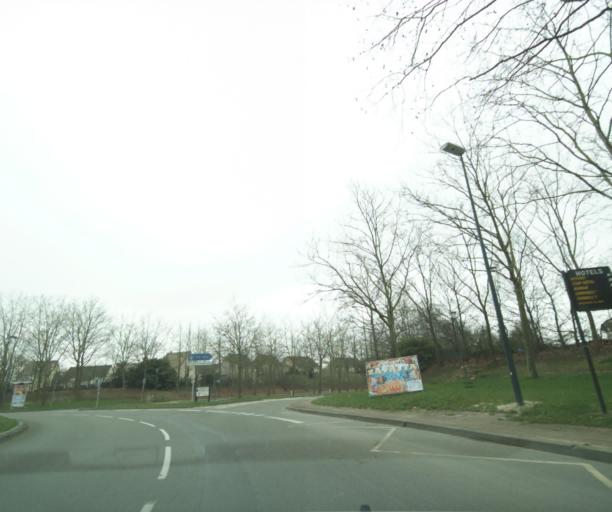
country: FR
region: Ile-de-France
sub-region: Departement du Val-d'Oise
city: Vaureal
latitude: 49.0473
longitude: 2.0234
